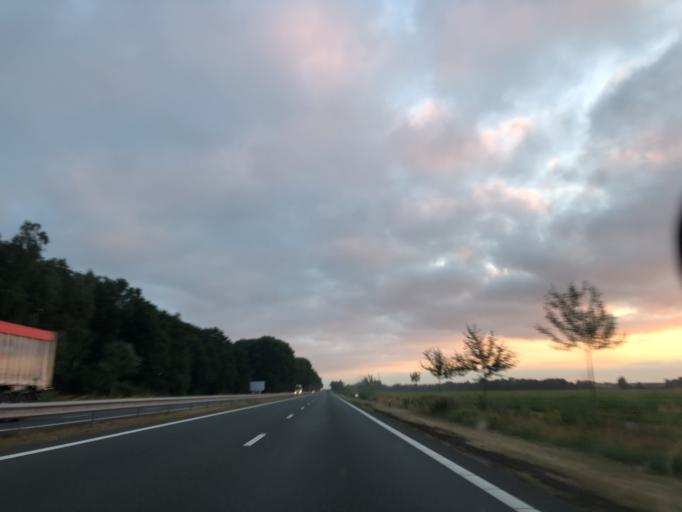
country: NL
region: Groningen
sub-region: Gemeente Veendam
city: Veendam
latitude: 53.1115
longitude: 6.8993
